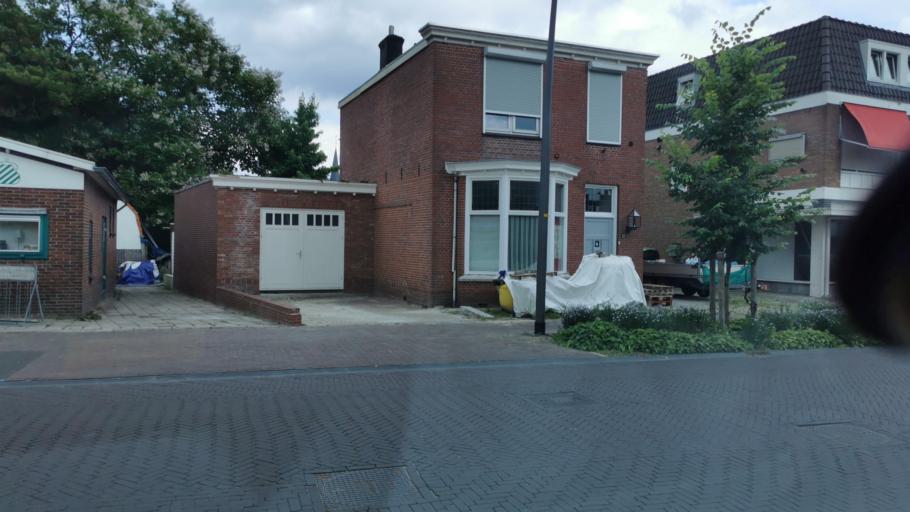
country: NL
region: Overijssel
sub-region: Gemeente Losser
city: Losser
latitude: 52.2621
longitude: 7.0047
